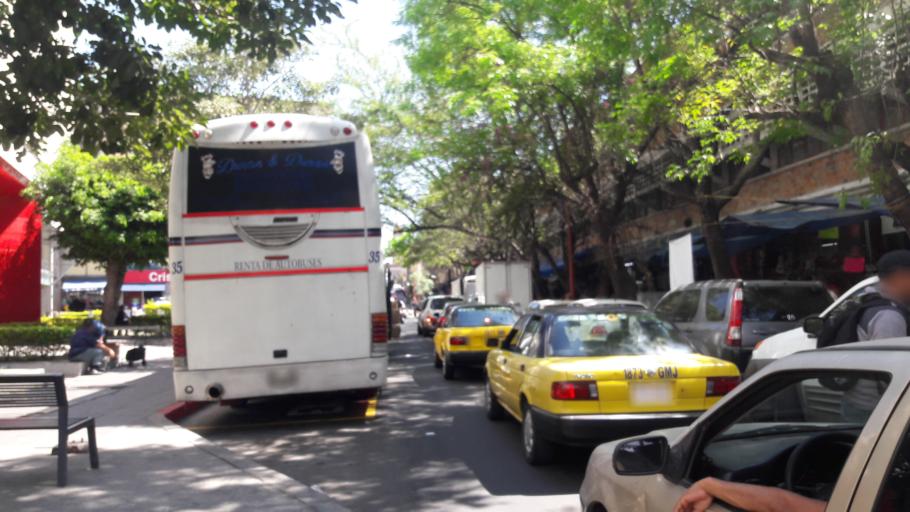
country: MX
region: Jalisco
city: Guadalajara
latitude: 20.6761
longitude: -103.3396
